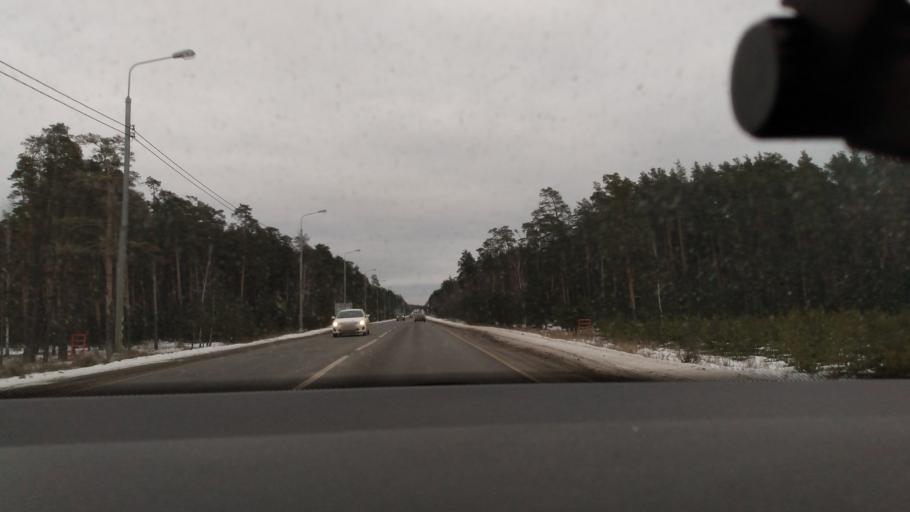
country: RU
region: Moskovskaya
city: Il'inskiy Pogost
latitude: 55.4885
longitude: 38.8854
